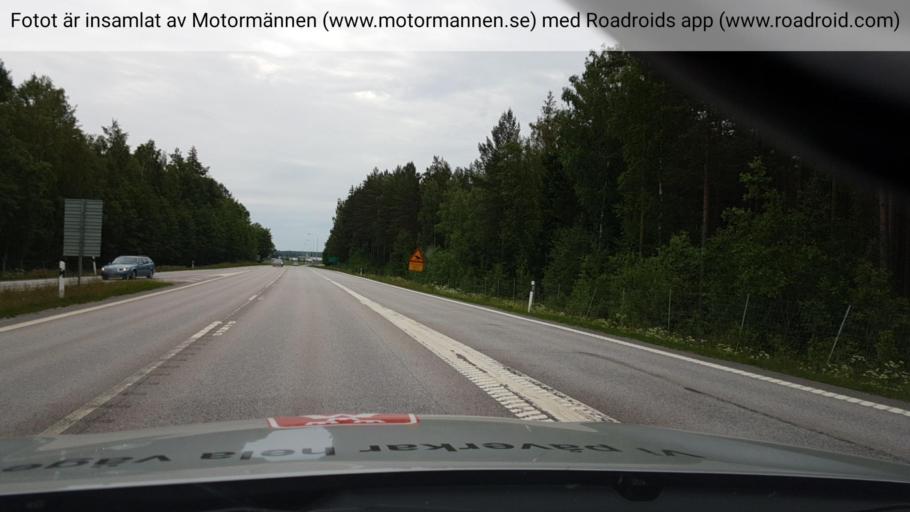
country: SE
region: OErebro
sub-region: Hallsbergs Kommun
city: Hallsberg
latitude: 59.1033
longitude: 15.0673
